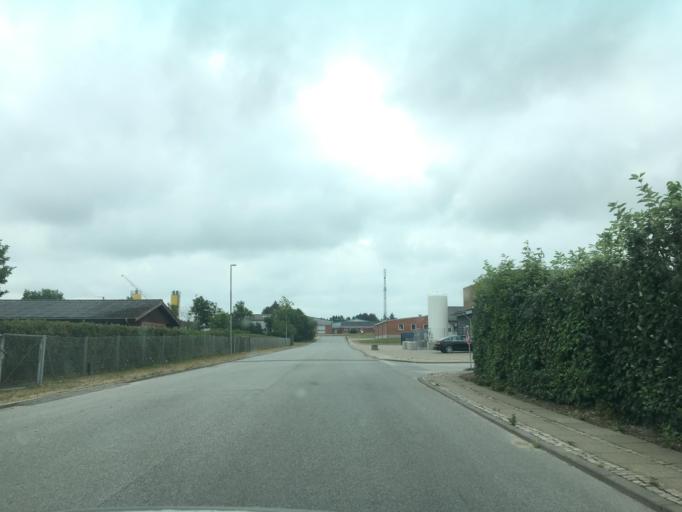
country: DK
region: North Denmark
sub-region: Thisted Kommune
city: Hurup
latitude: 56.7510
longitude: 8.4293
